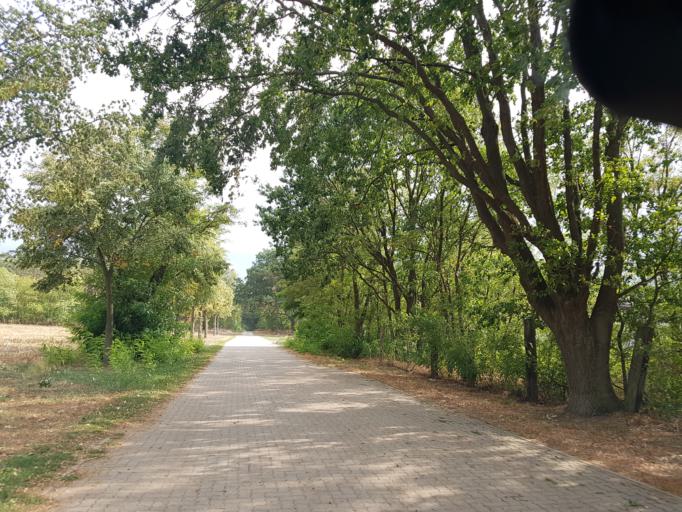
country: DE
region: Saxony-Anhalt
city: Rosslau
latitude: 52.0321
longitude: 12.2851
